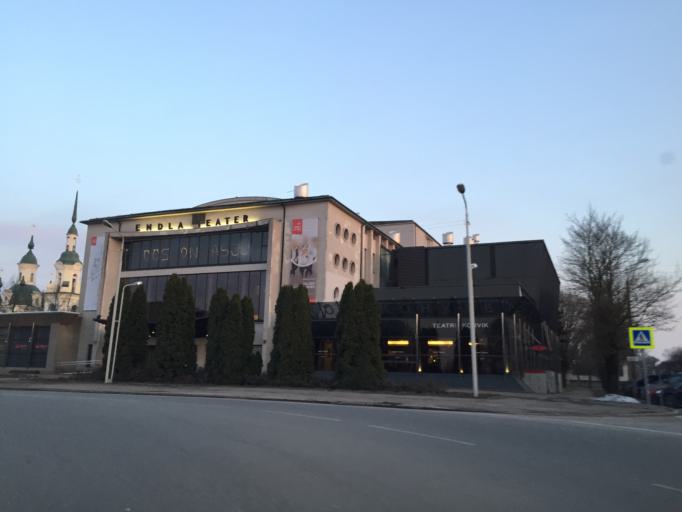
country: EE
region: Paernumaa
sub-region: Paernu linn
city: Parnu
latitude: 58.3859
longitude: 24.4960
